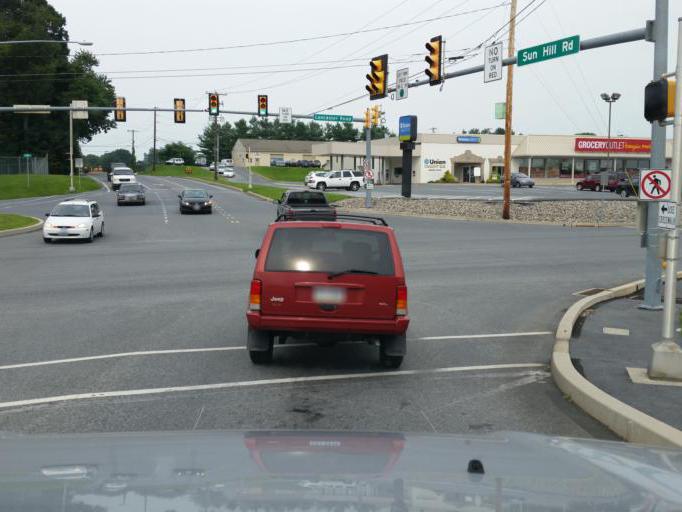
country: US
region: Pennsylvania
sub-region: Lancaster County
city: Manheim
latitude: 40.1498
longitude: -76.3817
